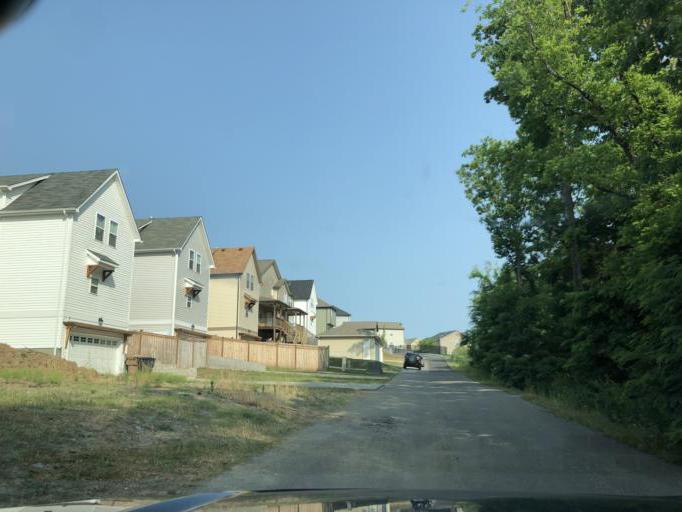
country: US
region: Tennessee
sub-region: Rutherford County
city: La Vergne
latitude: 36.0488
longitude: -86.6413
